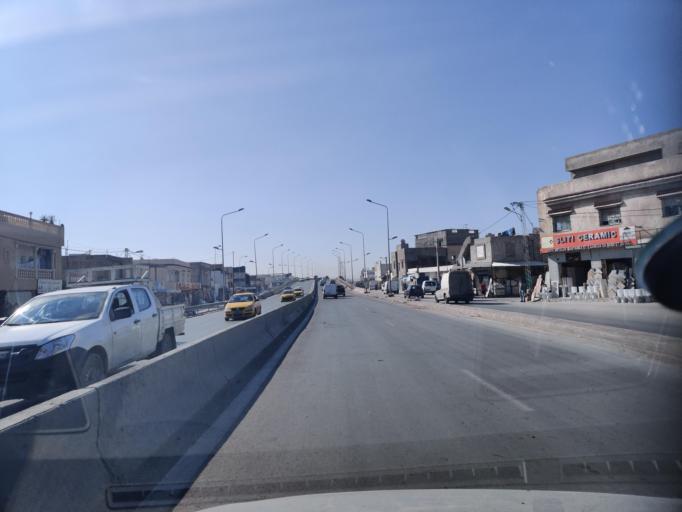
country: TN
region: Manouba
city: Manouba
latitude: 36.7932
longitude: 10.1191
